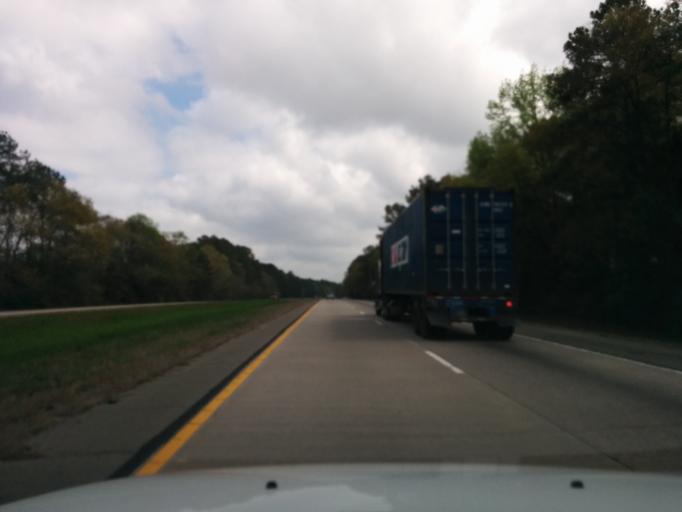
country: US
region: Georgia
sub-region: Bryan County
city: Pembroke
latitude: 32.2128
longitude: -81.5100
